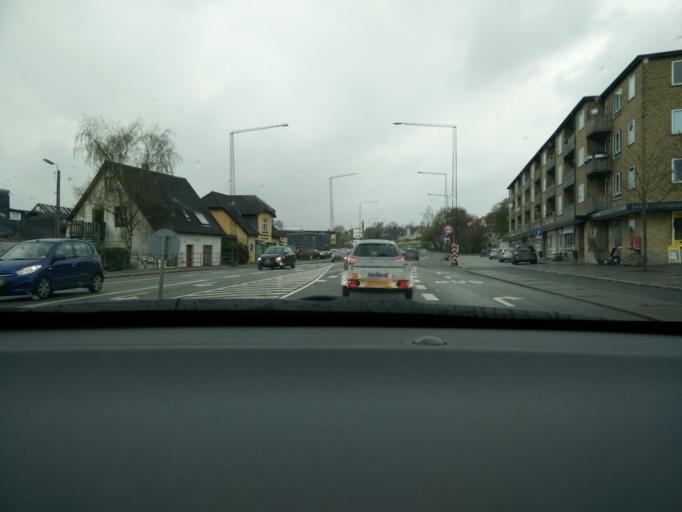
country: DK
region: Central Jutland
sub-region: Arhus Kommune
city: Arhus
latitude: 56.1674
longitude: 10.1634
